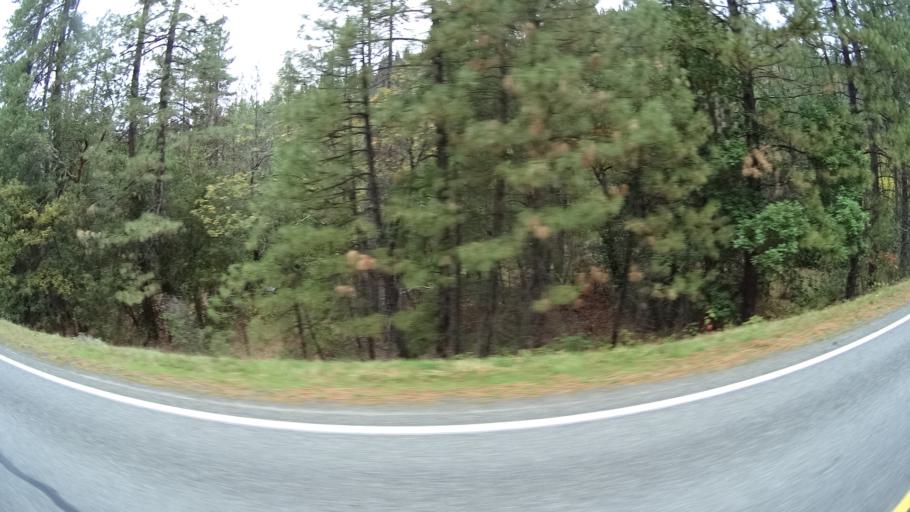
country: US
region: California
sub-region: Siskiyou County
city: Happy Camp
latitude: 41.8345
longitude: -123.1788
